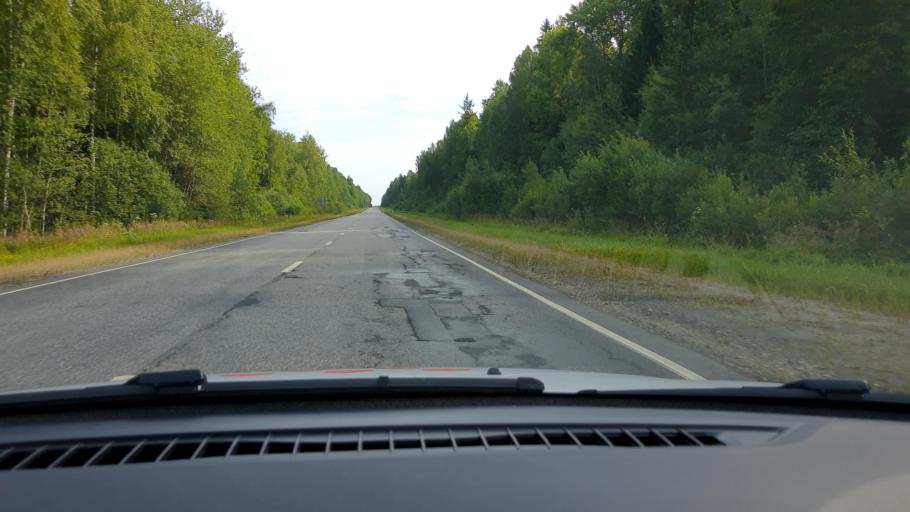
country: RU
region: Nizjnij Novgorod
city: Vladimirskoye
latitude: 56.9342
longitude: 45.0720
